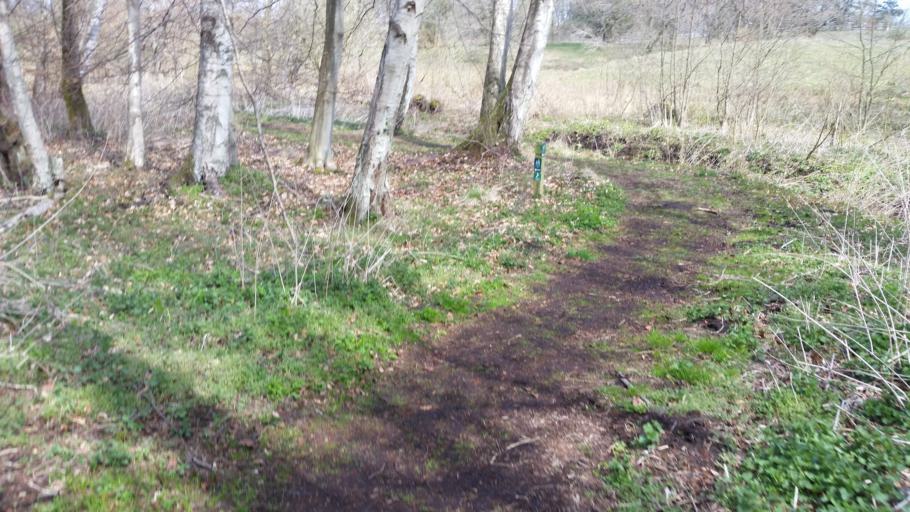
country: DK
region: Capital Region
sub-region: Helsingor Kommune
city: Hornbaek
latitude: 56.0755
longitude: 12.4099
